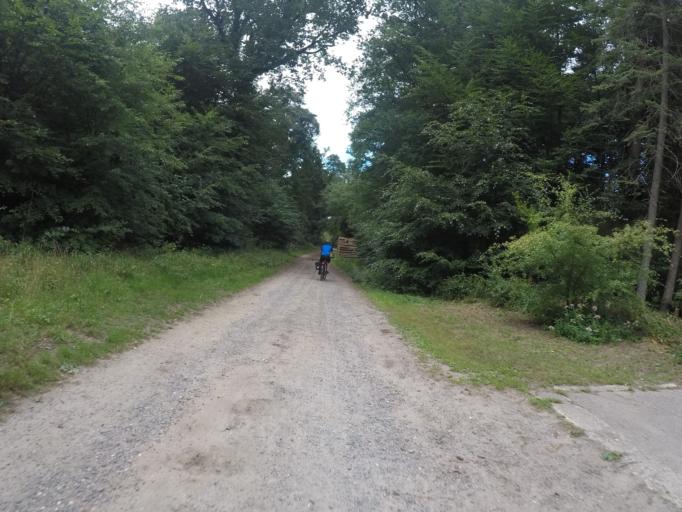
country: DE
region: Lower Saxony
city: Wingst
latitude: 53.7374
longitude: 9.0723
